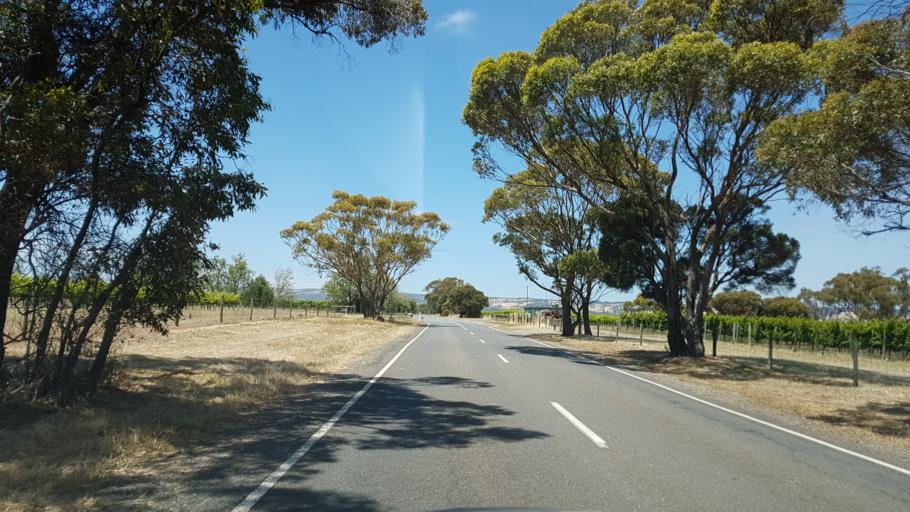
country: AU
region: South Australia
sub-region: Onkaparinga
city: McLaren Vale
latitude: -35.2313
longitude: 138.5178
